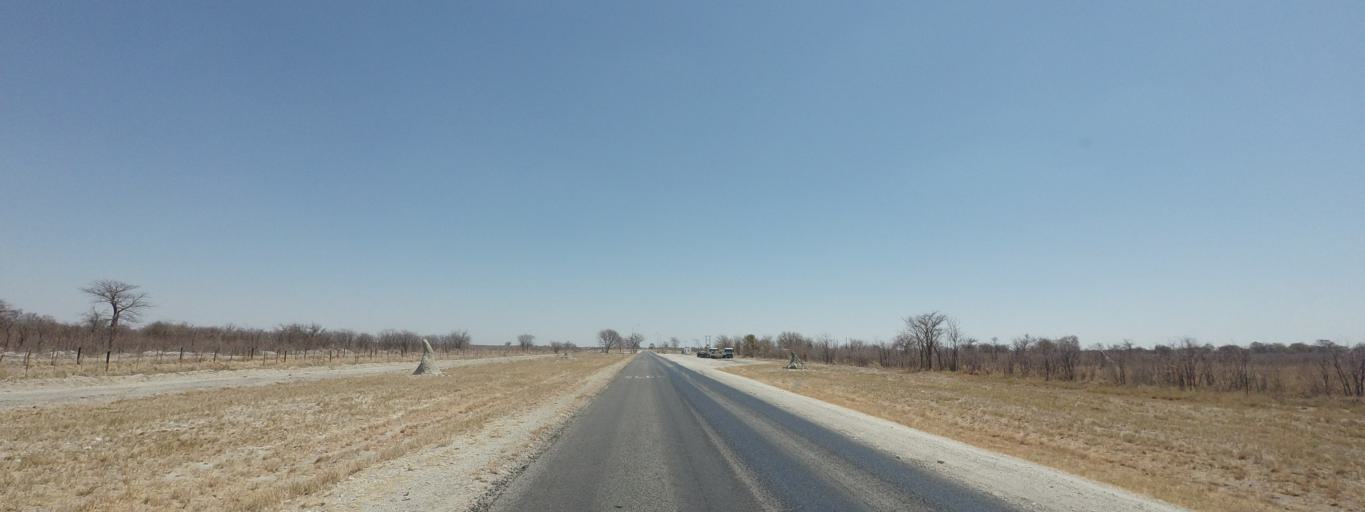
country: BW
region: Central
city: Nata
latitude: -20.3171
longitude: 26.3087
